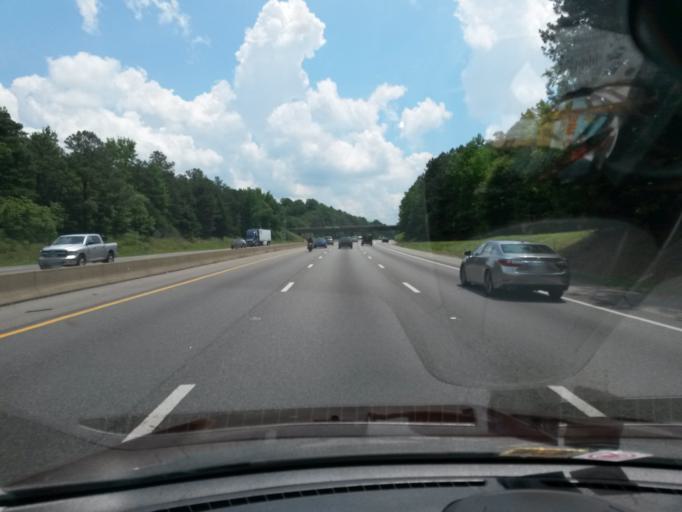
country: US
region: Virginia
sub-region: Chesterfield County
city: Chester
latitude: 37.3765
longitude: -77.4077
